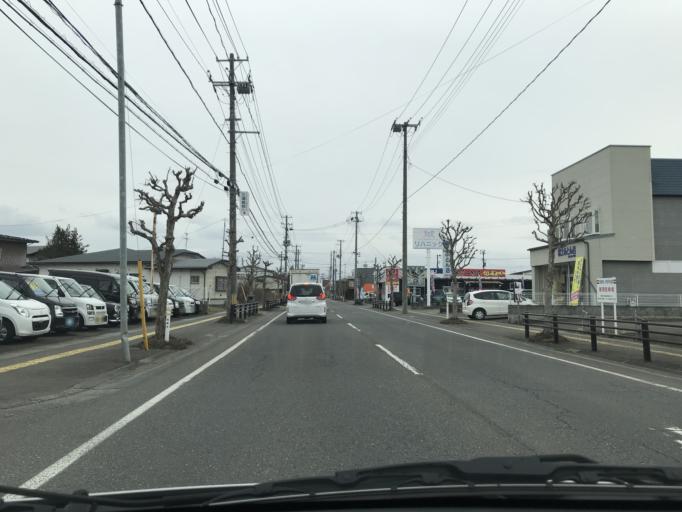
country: JP
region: Iwate
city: Hanamaki
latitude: 39.3911
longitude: 141.1082
